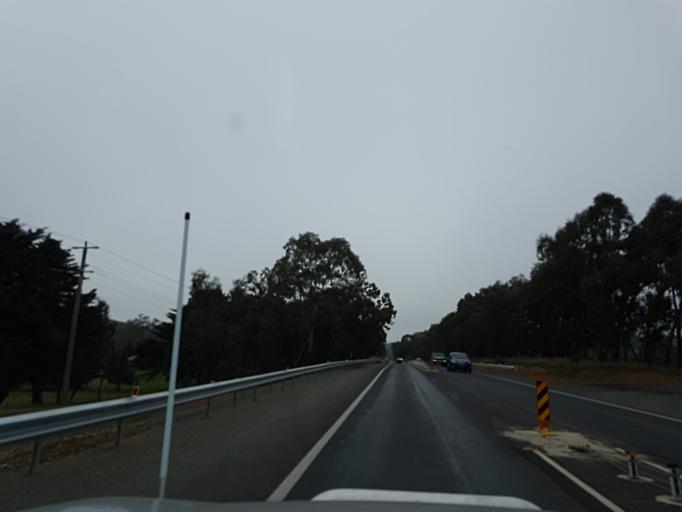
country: AU
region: Victoria
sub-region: Murrindindi
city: Alexandra
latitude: -37.2105
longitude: 145.4517
